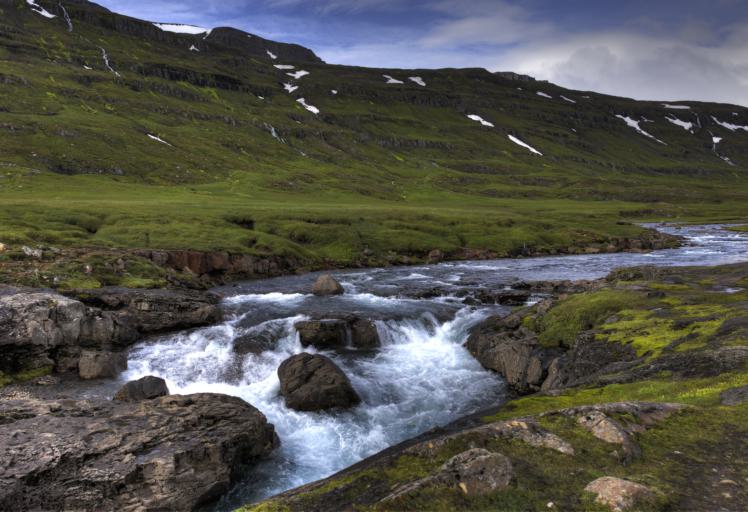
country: IS
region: East
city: Eskifjoerdur
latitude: 65.2308
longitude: -14.0806
